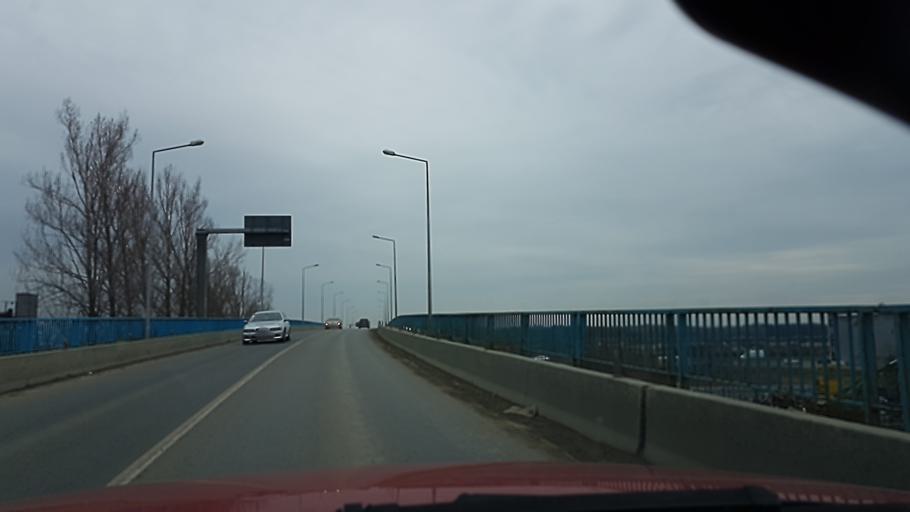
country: RO
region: Ilfov
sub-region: Comuna Tunari
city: Tunari
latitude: 44.5374
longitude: 26.1426
